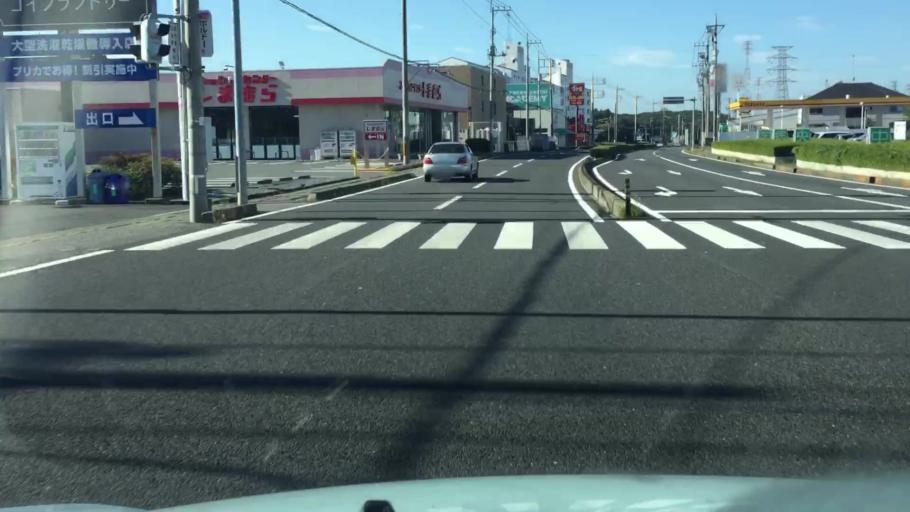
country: JP
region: Tochigi
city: Ujiie
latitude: 36.6185
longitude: 139.9905
